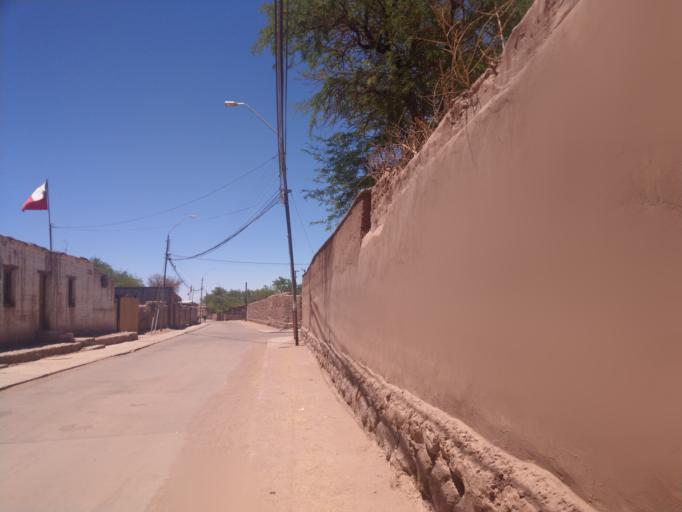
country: CL
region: Antofagasta
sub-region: Provincia de El Loa
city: San Pedro de Atacama
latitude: -22.9129
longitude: -68.2011
